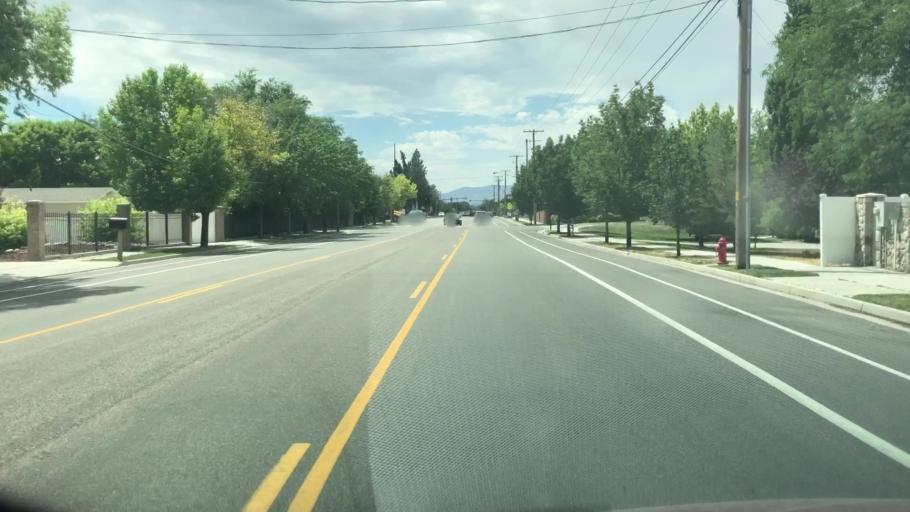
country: US
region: Utah
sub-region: Salt Lake County
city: South Jordan
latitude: 40.5470
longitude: -111.9292
